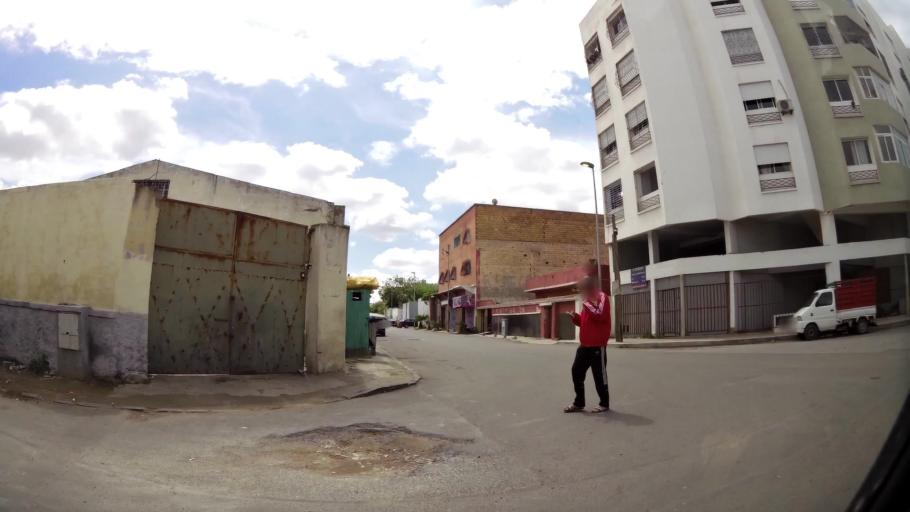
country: MA
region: Grand Casablanca
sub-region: Casablanca
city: Casablanca
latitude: 33.6201
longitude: -7.5469
